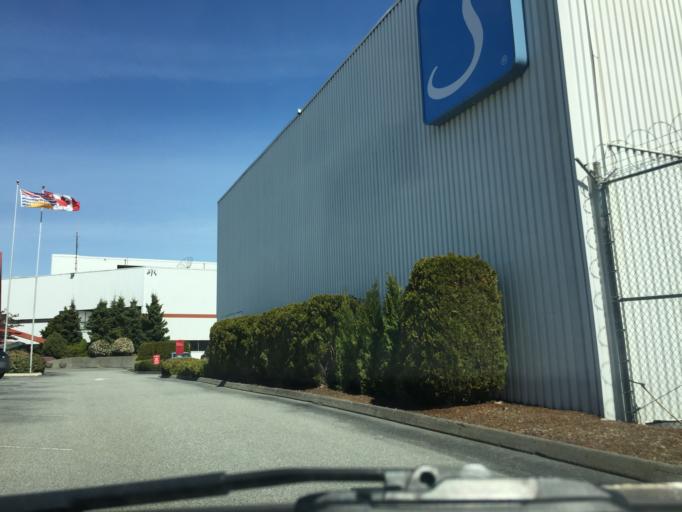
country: CA
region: British Columbia
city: Richmond
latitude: 49.1804
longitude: -123.1648
